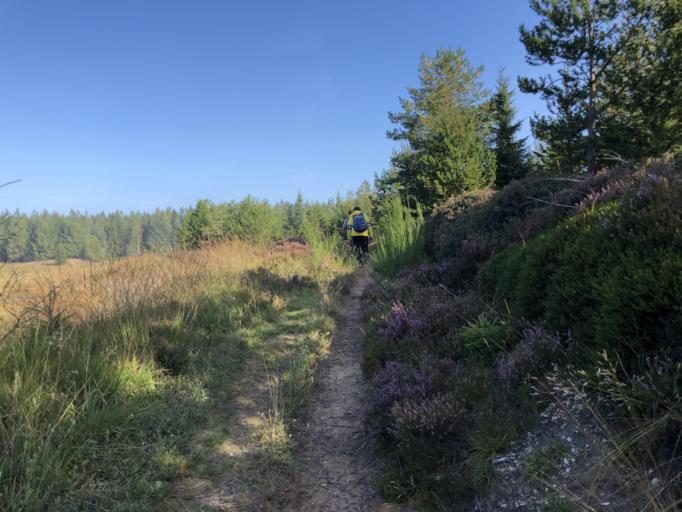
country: DK
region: Central Jutland
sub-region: Lemvig Kommune
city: Lemvig
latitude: 56.4751
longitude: 8.3338
